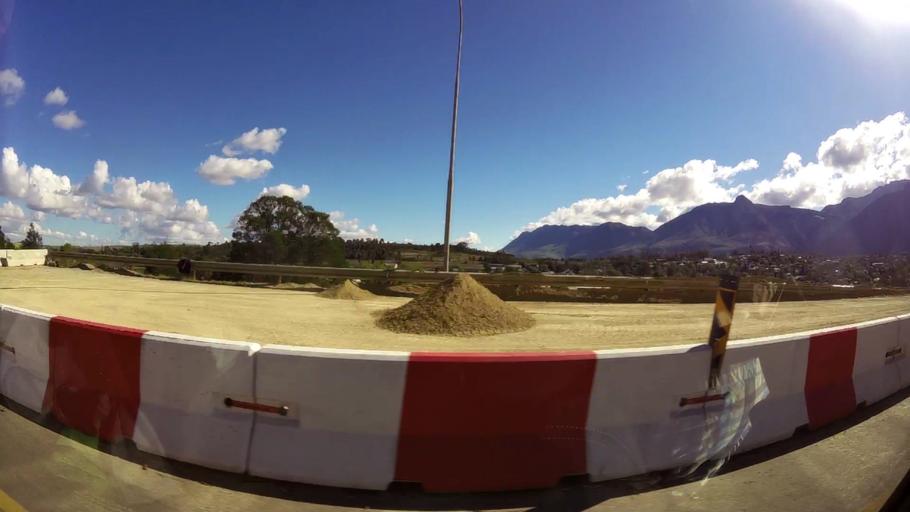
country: ZA
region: Western Cape
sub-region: Overberg District Municipality
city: Swellendam
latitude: -34.0327
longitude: 20.4376
